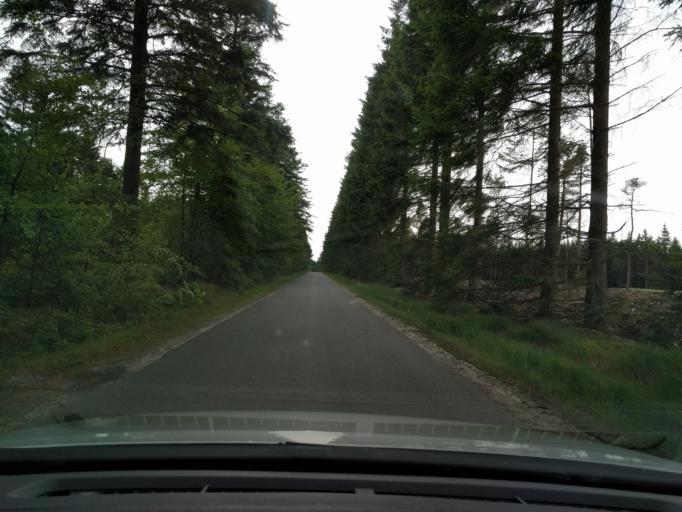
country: DK
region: Central Jutland
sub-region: Herning Kommune
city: Kibaek
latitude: 56.0376
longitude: 8.9314
